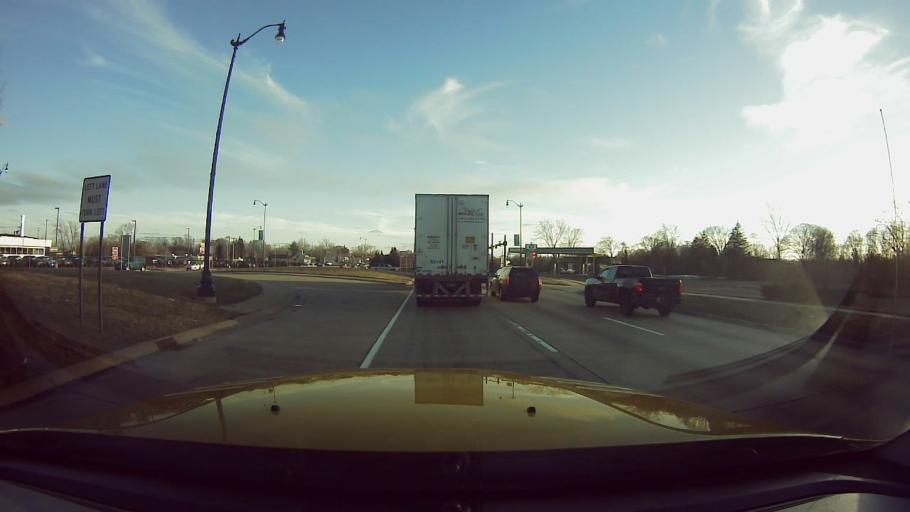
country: US
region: Michigan
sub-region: Wayne County
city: Taylor
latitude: 42.2287
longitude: -83.2694
